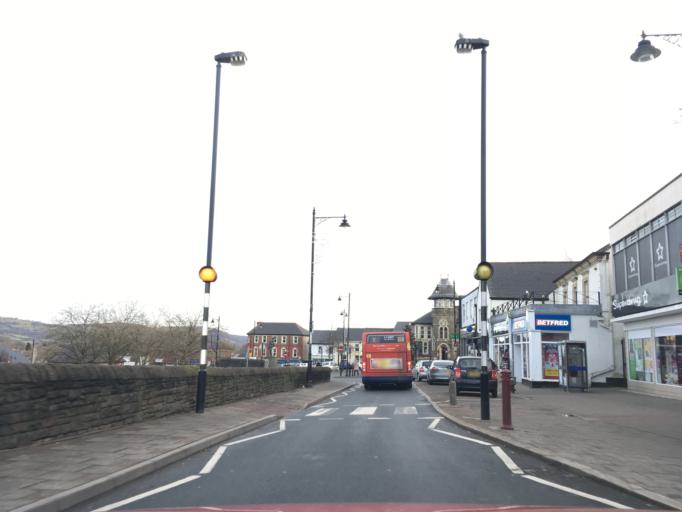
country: GB
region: Wales
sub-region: Caerphilly County Borough
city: Caerphilly
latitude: 51.5745
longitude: -3.2193
